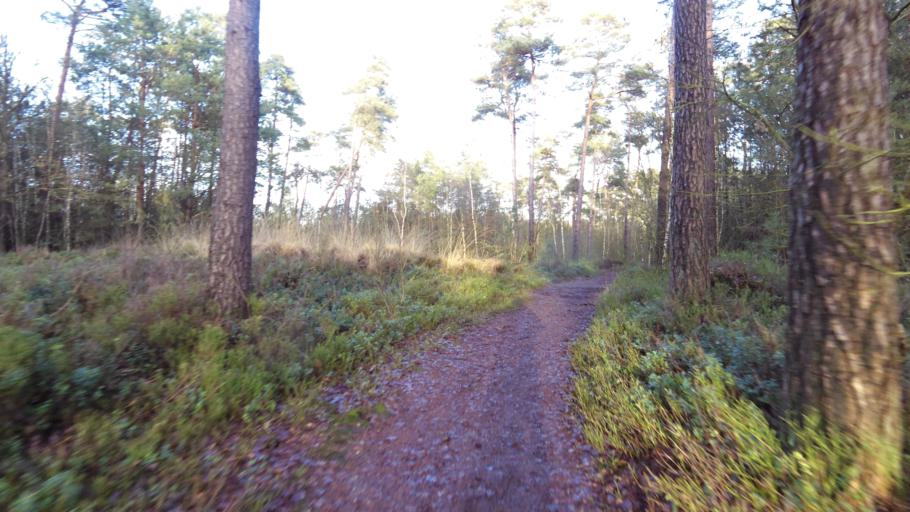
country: NL
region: Gelderland
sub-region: Gemeente Epe
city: Vaassen
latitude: 52.2966
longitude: 5.9250
